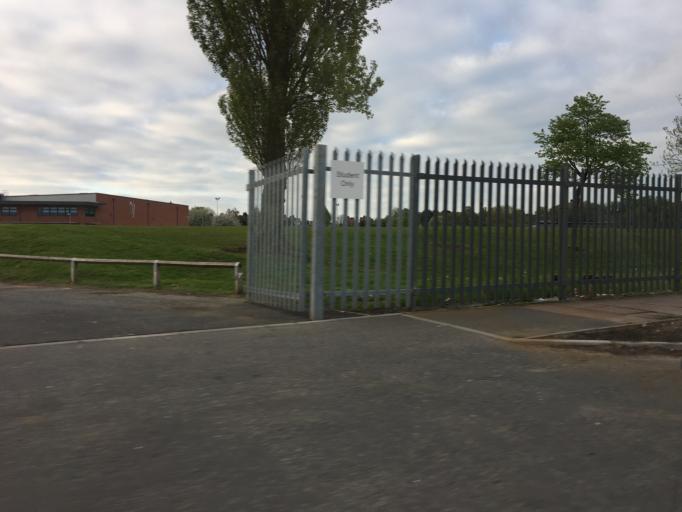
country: GB
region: England
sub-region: Leicestershire
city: Oadby
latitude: 52.6265
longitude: -1.0911
